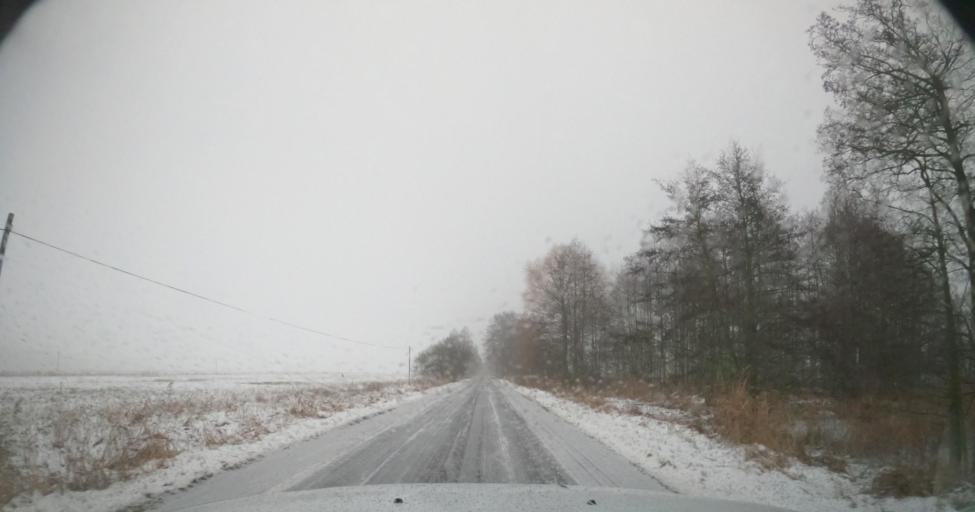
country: PL
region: West Pomeranian Voivodeship
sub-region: Powiat policki
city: Police
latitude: 53.5594
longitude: 14.6497
